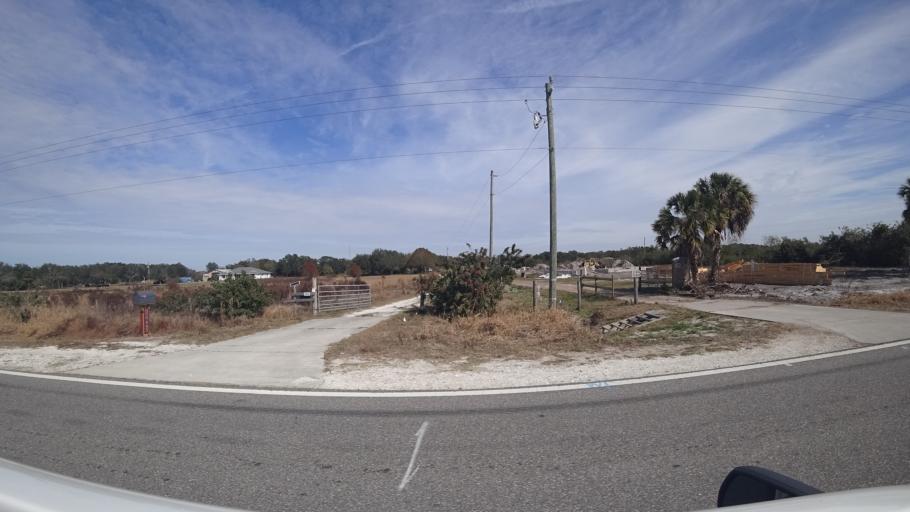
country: US
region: Florida
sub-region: Hillsborough County
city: Sun City Center
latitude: 27.5682
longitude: -82.3806
